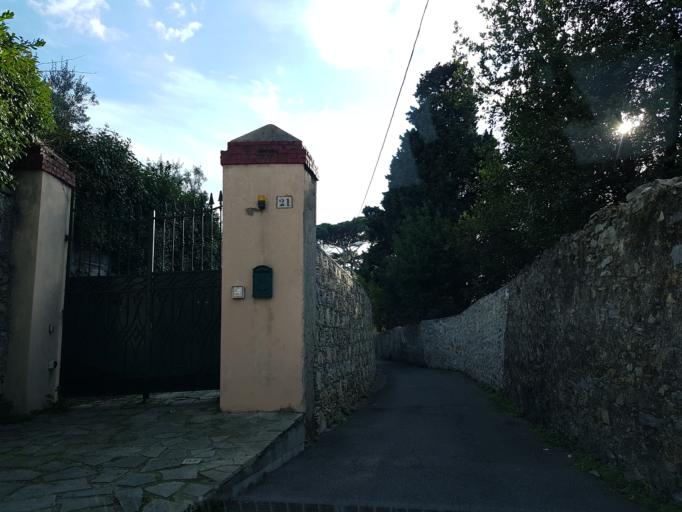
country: IT
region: Liguria
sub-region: Provincia di Genova
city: Genoa
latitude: 44.3982
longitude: 8.9829
